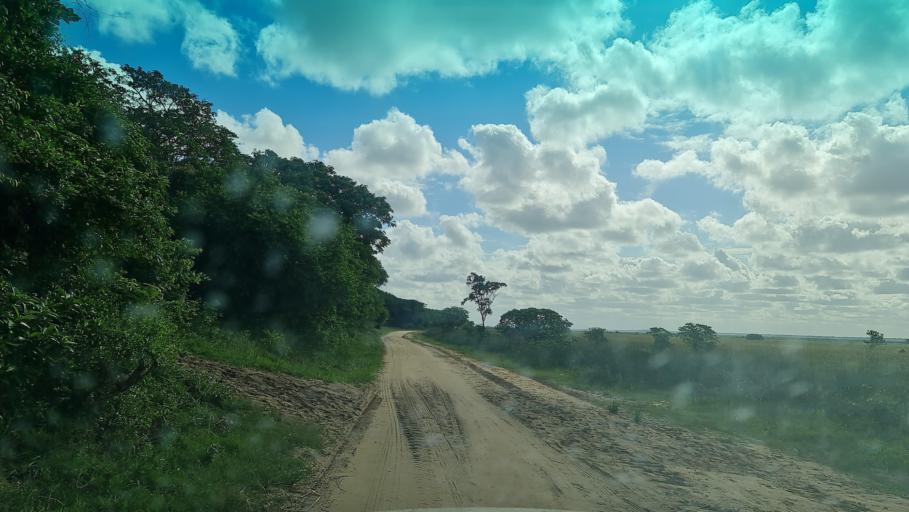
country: MZ
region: Maputo
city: Manhica
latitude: -25.4318
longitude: 32.8906
